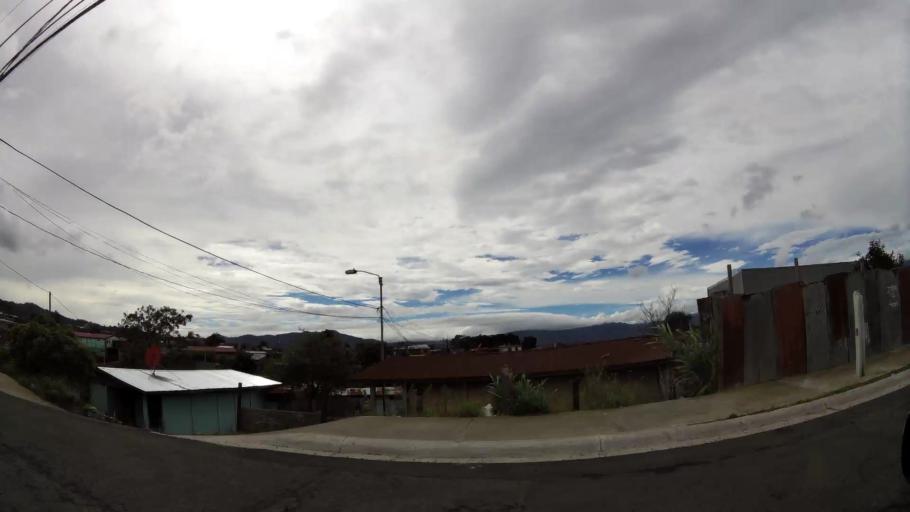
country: CR
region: San Jose
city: Ipis
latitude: 9.9602
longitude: -84.0102
